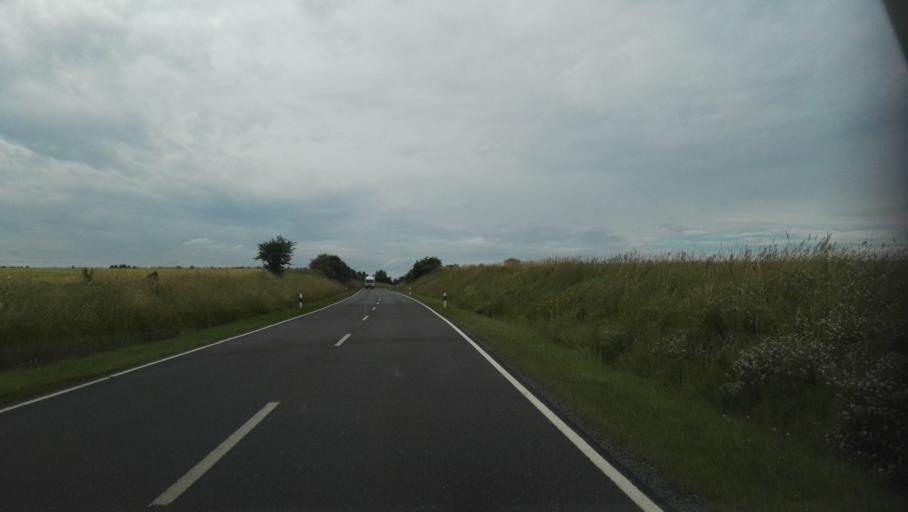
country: DE
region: Bavaria
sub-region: Upper Franconia
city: Hollfeld
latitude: 49.9194
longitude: 11.3091
